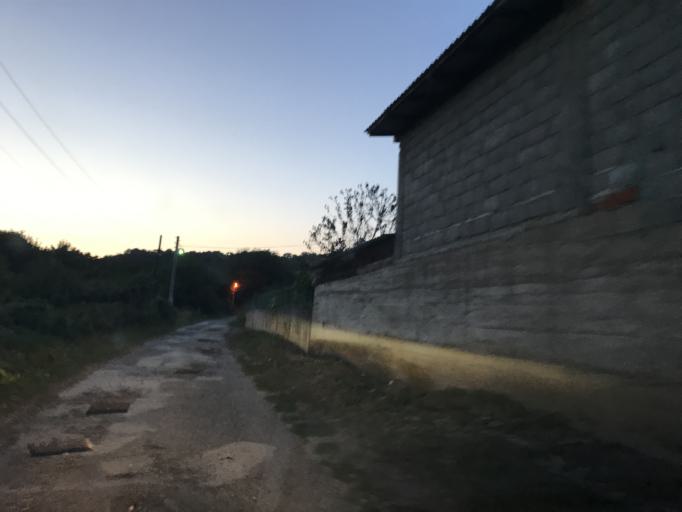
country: BG
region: Vidin
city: Bregovo
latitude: 44.1222
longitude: 22.5699
